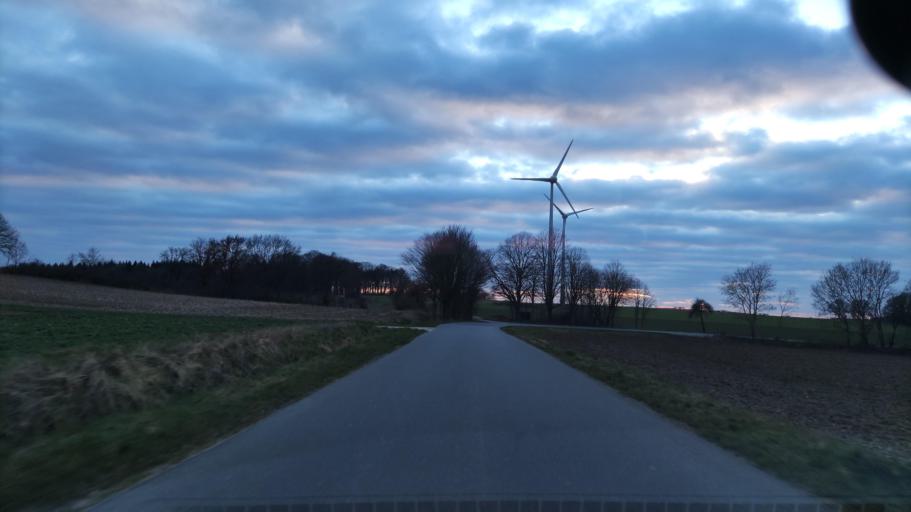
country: DE
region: Lower Saxony
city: Natendorf
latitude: 53.0521
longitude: 10.4698
